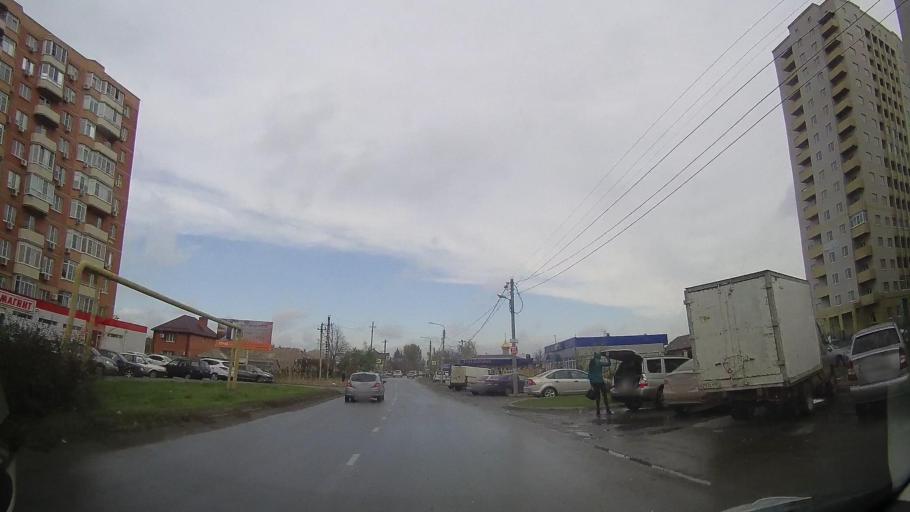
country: RU
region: Rostov
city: Bataysk
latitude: 47.1376
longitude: 39.7677
